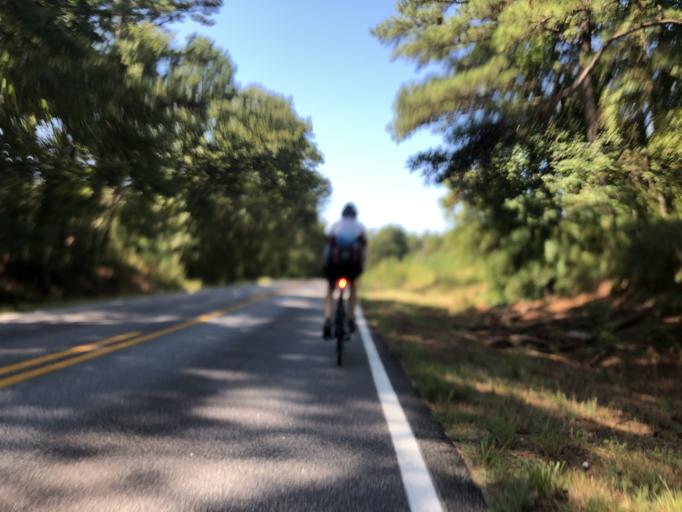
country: US
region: Georgia
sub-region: Coweta County
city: Newnan
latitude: 33.4046
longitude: -84.9540
